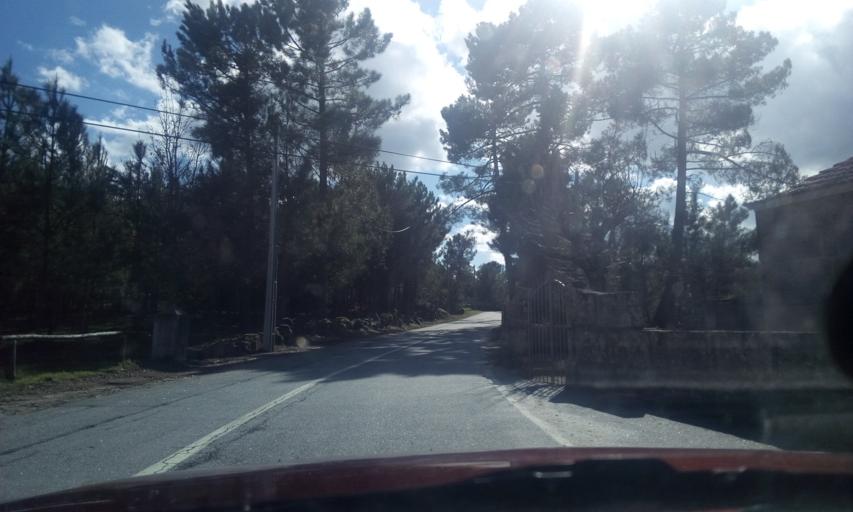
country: PT
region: Guarda
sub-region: Fornos de Algodres
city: Fornos de Algodres
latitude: 40.6443
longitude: -7.5225
